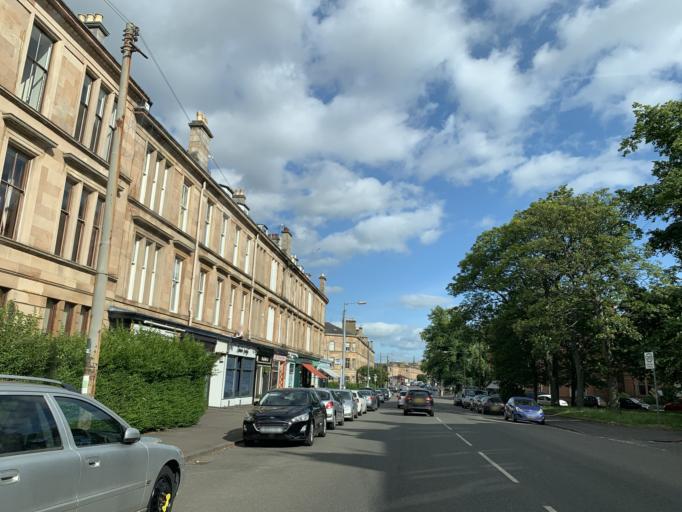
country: GB
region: Scotland
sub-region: Glasgow City
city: Glasgow
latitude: 55.8392
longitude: -4.2756
